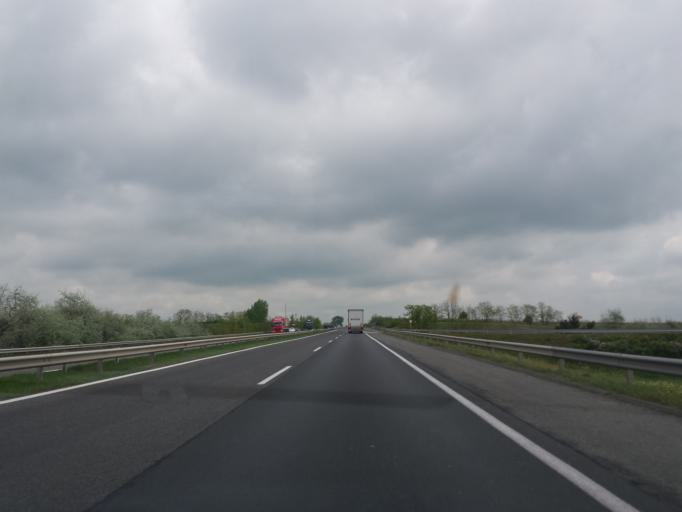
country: HU
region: Gyor-Moson-Sopron
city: Toltestava
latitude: 47.6492
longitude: 17.7106
